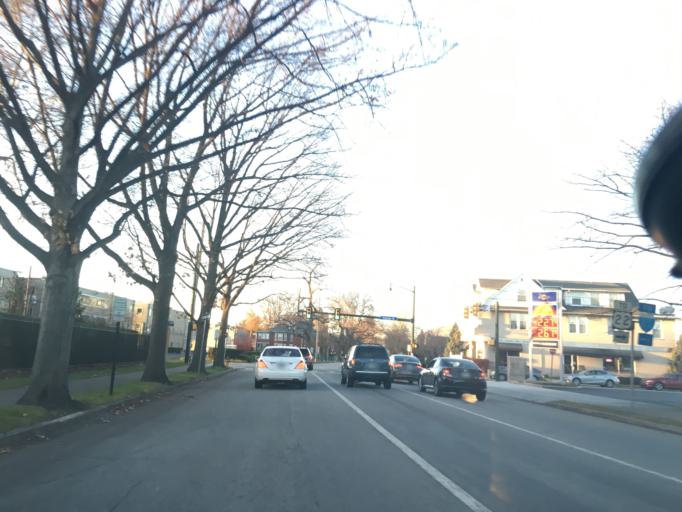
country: US
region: Pennsylvania
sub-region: Dauphin County
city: Harrisburg
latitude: 40.2779
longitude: -76.8983
